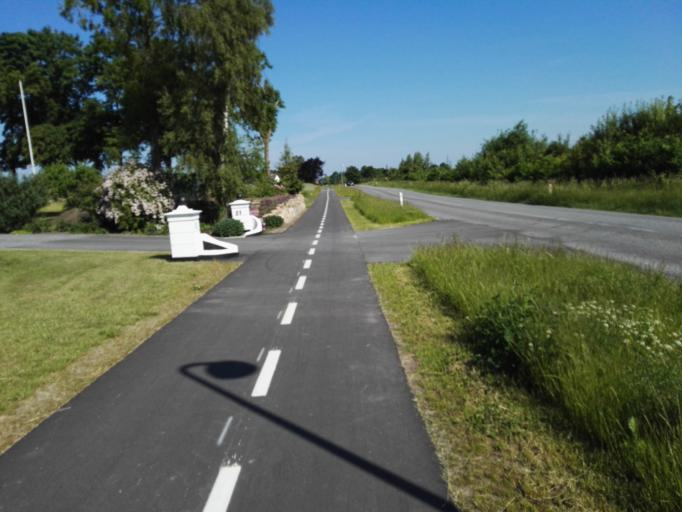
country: DK
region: Zealand
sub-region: Lejre Kommune
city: Ejby
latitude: 55.7122
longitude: 11.8950
